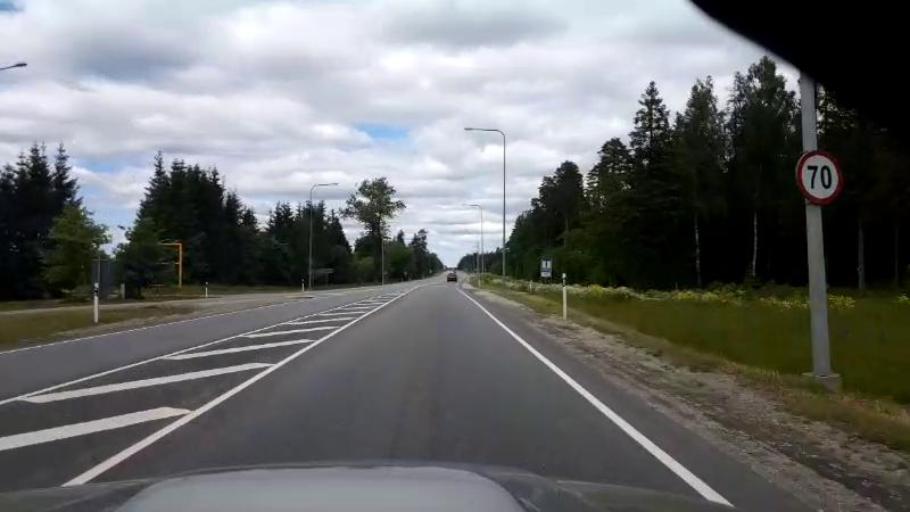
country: EE
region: Raplamaa
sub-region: Maerjamaa vald
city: Marjamaa
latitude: 58.9254
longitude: 24.4602
